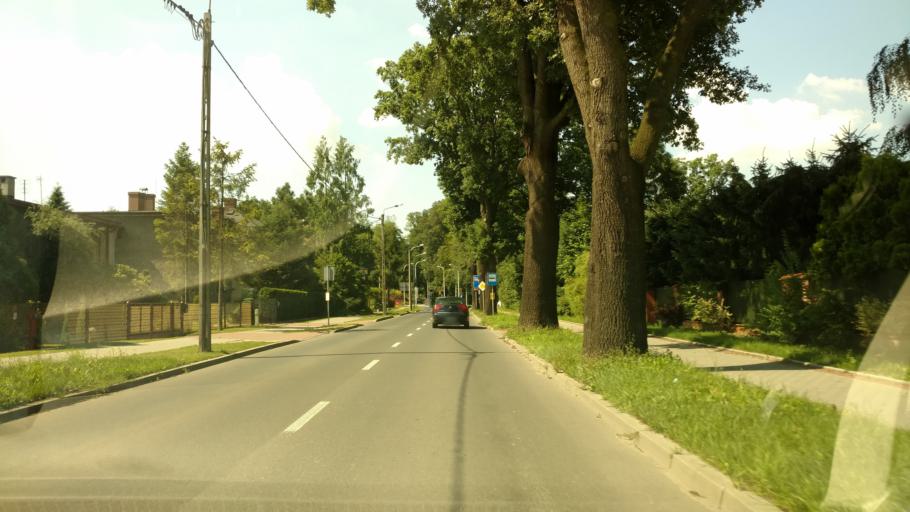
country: PL
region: Silesian Voivodeship
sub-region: Powiat pszczynski
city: Pszczyna
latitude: 49.9868
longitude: 18.9492
